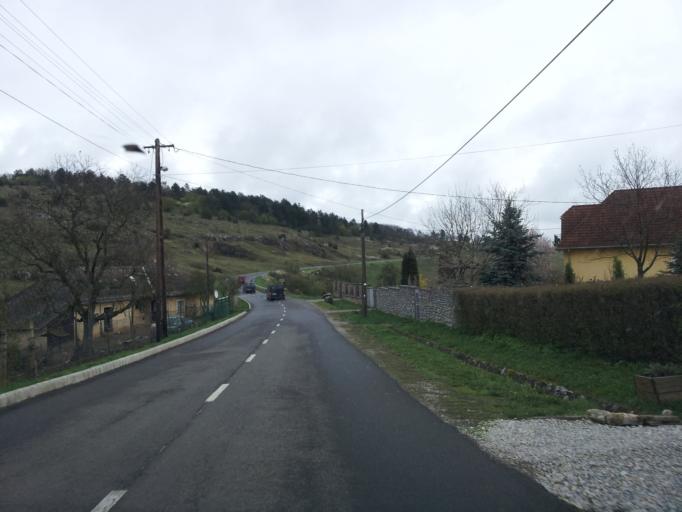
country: HU
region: Borsod-Abauj-Zemplen
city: Rudabanya
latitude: 48.4691
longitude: 20.5102
